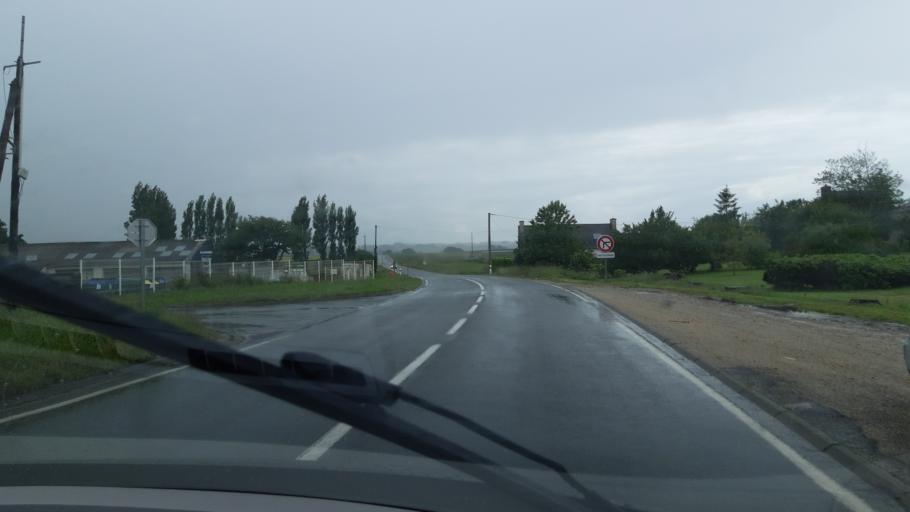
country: FR
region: Brittany
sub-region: Departement du Finistere
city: Plougoulm
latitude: 48.6441
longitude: -4.0490
